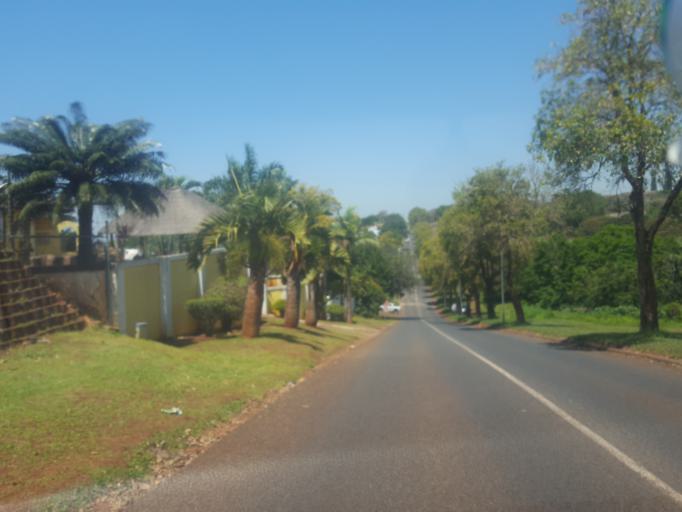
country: ZA
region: KwaZulu-Natal
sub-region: uThungulu District Municipality
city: Empangeni
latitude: -28.7503
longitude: 31.9023
